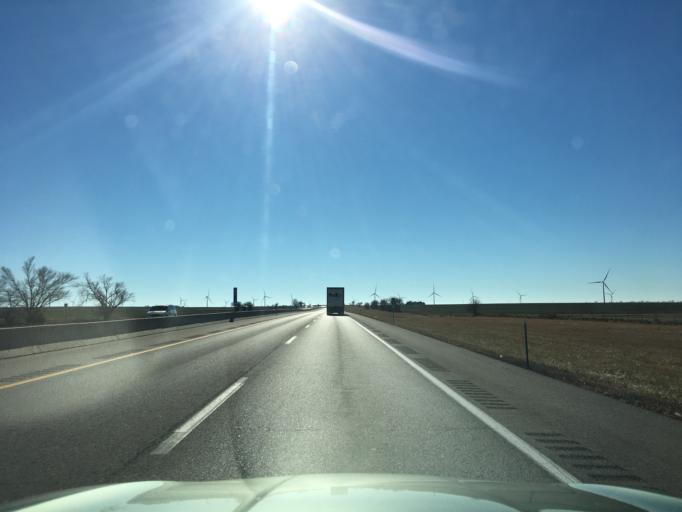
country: US
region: Kansas
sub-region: Sumner County
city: Wellington
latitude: 37.1731
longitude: -97.3396
